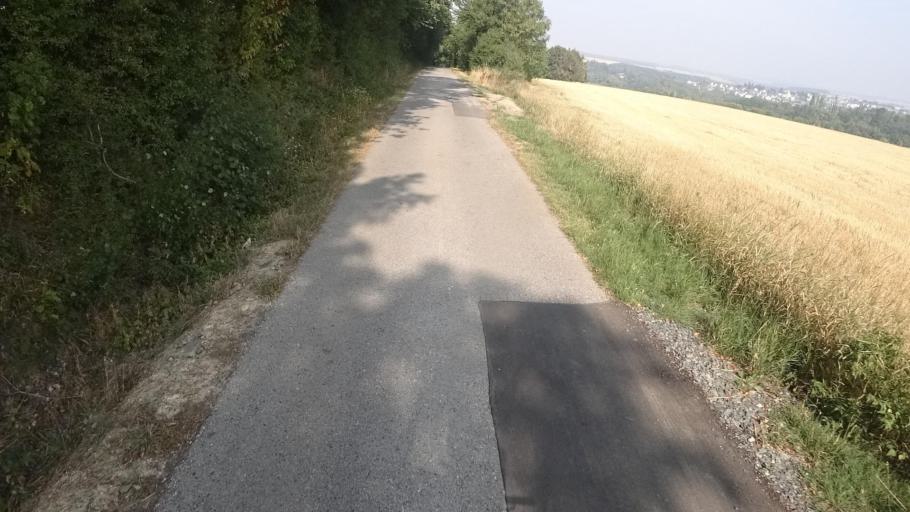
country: DE
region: Rheinland-Pfalz
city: Simmern
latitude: 49.9705
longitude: 7.5237
